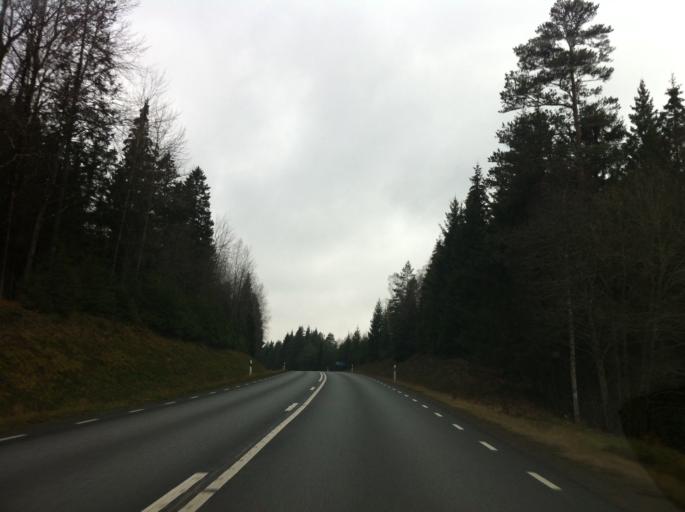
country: SE
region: Joenkoeping
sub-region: Vetlanda Kommun
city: Landsbro
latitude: 57.3944
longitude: 14.8212
